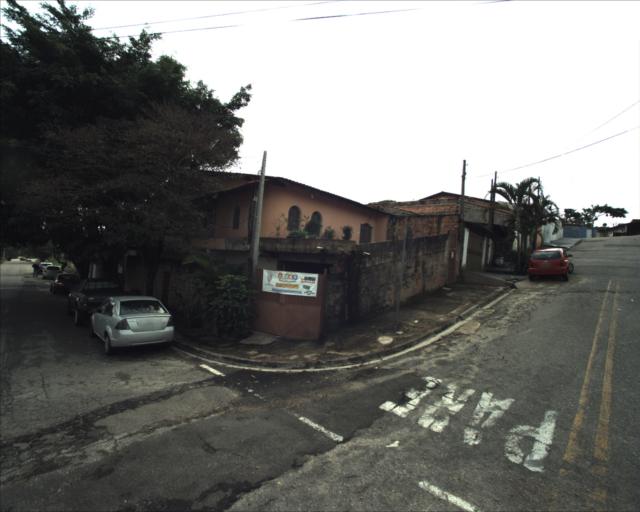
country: BR
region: Sao Paulo
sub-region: Sorocaba
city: Sorocaba
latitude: -23.5061
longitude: -47.4971
